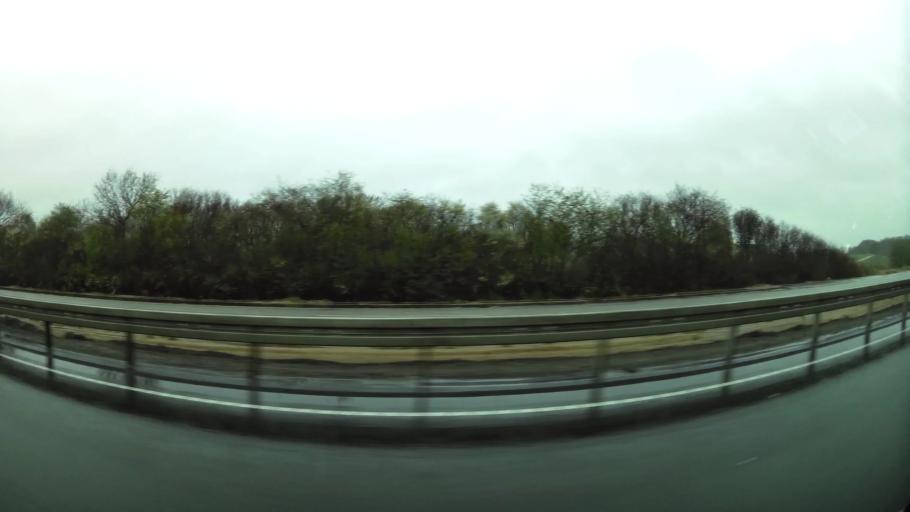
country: DK
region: Central Jutland
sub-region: Herning Kommune
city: Avlum
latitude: 56.2252
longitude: 8.8287
